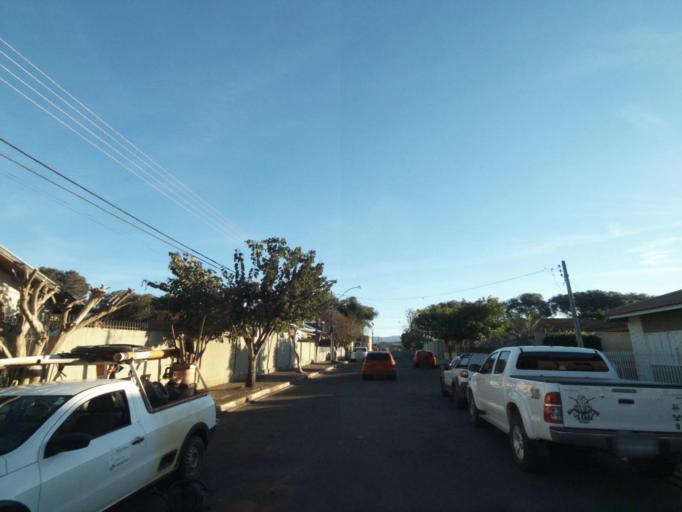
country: BR
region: Parana
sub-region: Tibagi
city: Tibagi
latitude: -24.5168
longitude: -50.4128
